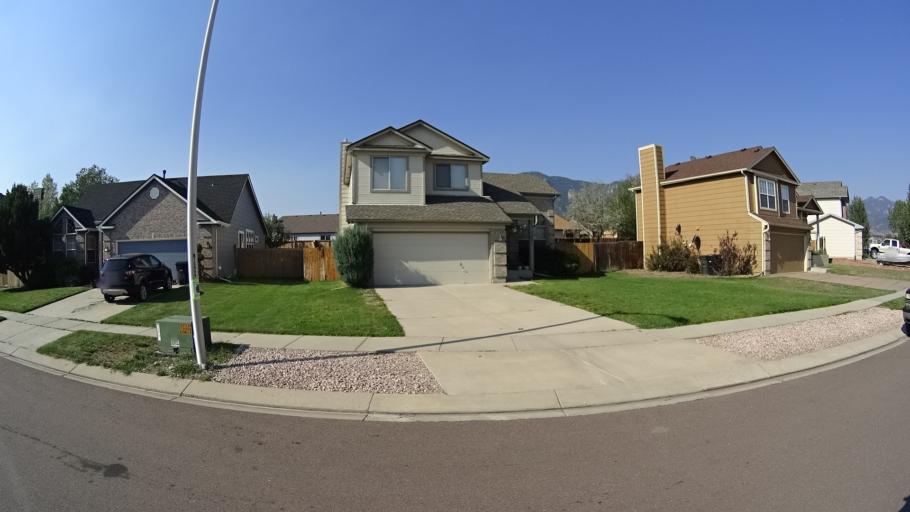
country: US
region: Colorado
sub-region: El Paso County
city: Stratmoor
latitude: 38.7711
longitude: -104.8023
